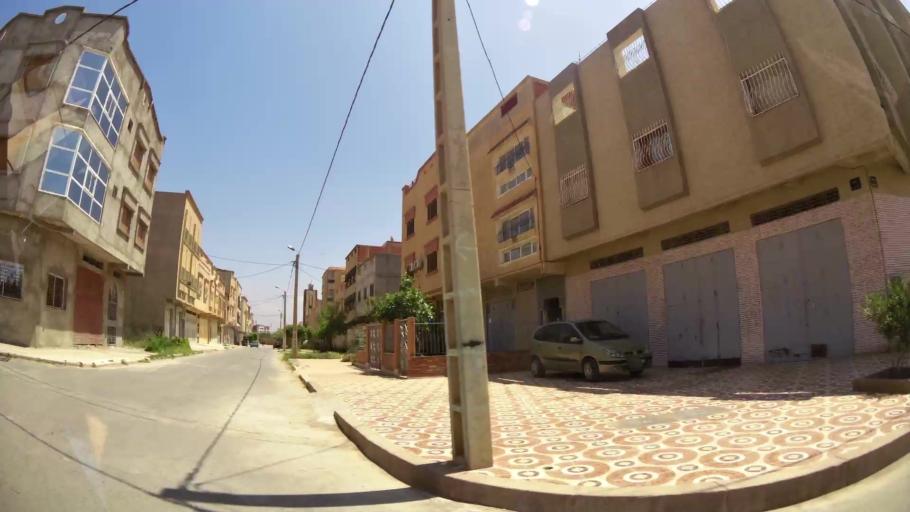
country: MA
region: Oriental
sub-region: Oujda-Angad
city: Oujda
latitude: 34.6957
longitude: -1.8975
